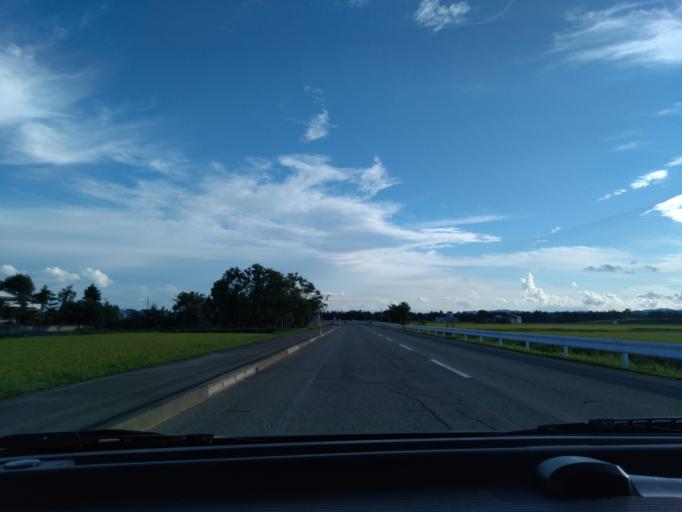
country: JP
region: Akita
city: Omagari
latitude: 39.4050
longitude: 140.4757
